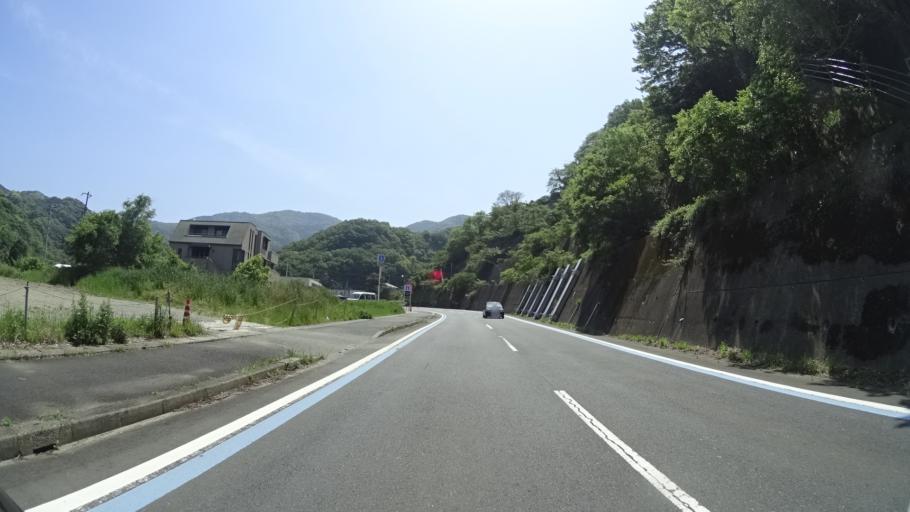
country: JP
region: Ehime
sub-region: Nishiuwa-gun
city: Ikata-cho
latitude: 33.3866
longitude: 132.1250
